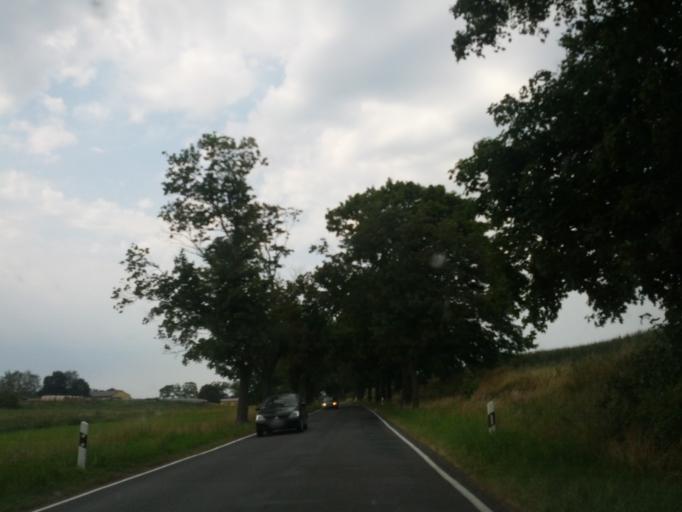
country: DE
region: Brandenburg
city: Kremmen
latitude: 52.7436
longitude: 12.9502
